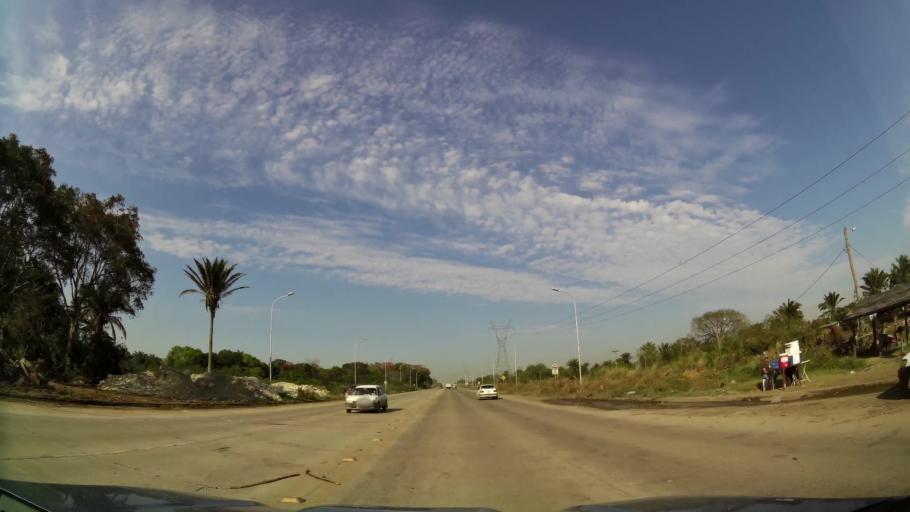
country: BO
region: Santa Cruz
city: Santa Cruz de la Sierra
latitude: -17.7159
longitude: -63.1280
